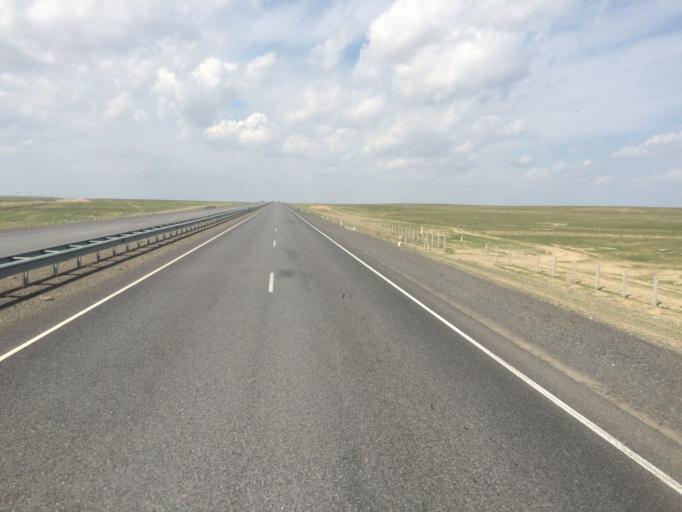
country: KZ
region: Qyzylorda
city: Shalqiya
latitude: 43.8586
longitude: 67.4012
